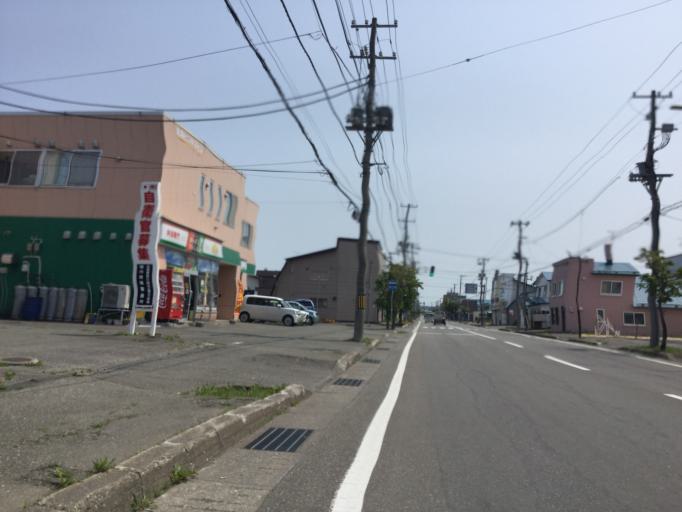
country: JP
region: Hokkaido
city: Wakkanai
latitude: 45.3963
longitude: 141.6910
